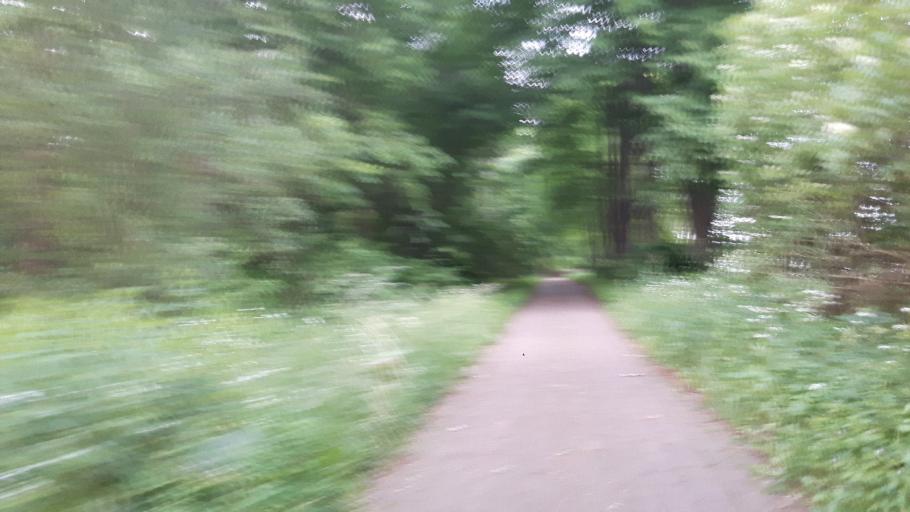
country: DE
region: Brandenburg
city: Gartz
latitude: 53.2232
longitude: 14.4072
